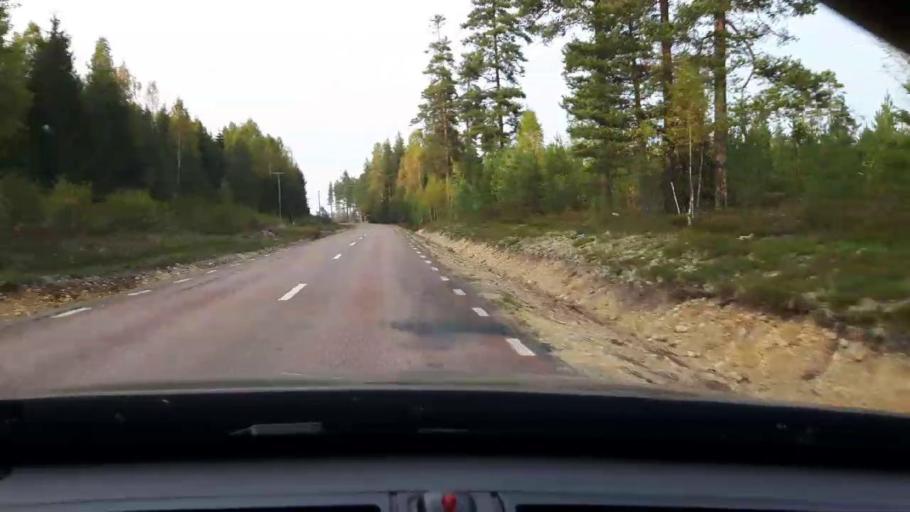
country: SE
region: Dalarna
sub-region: Gagnefs Kommun
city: Mockfjard
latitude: 60.3083
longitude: 14.9445
